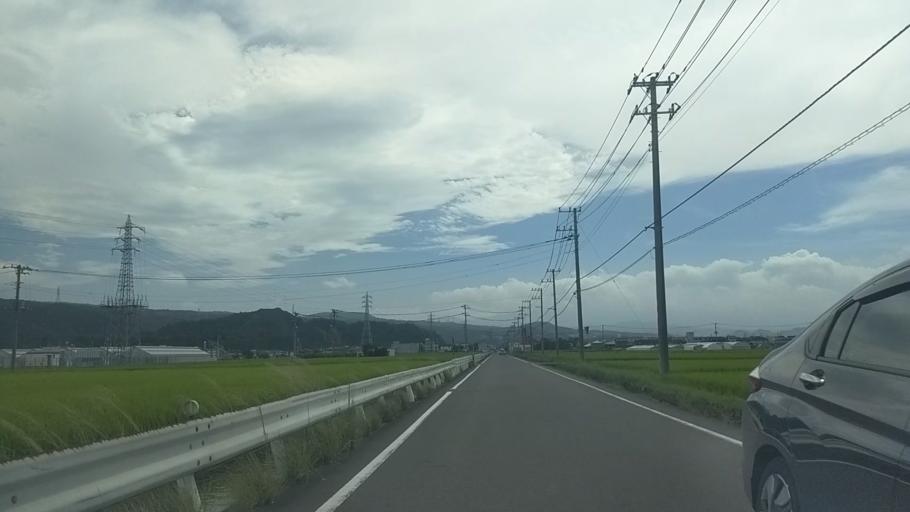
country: JP
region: Shizuoka
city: Mishima
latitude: 35.0638
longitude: 138.9467
